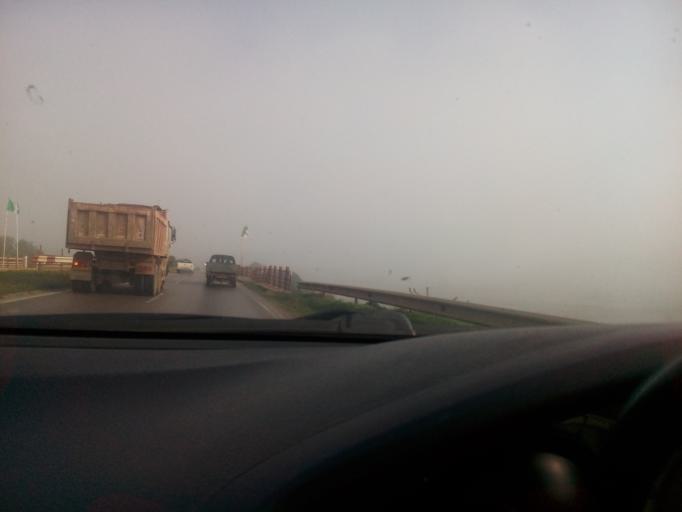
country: DZ
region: Oran
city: Es Senia
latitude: 35.6162
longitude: -0.7205
